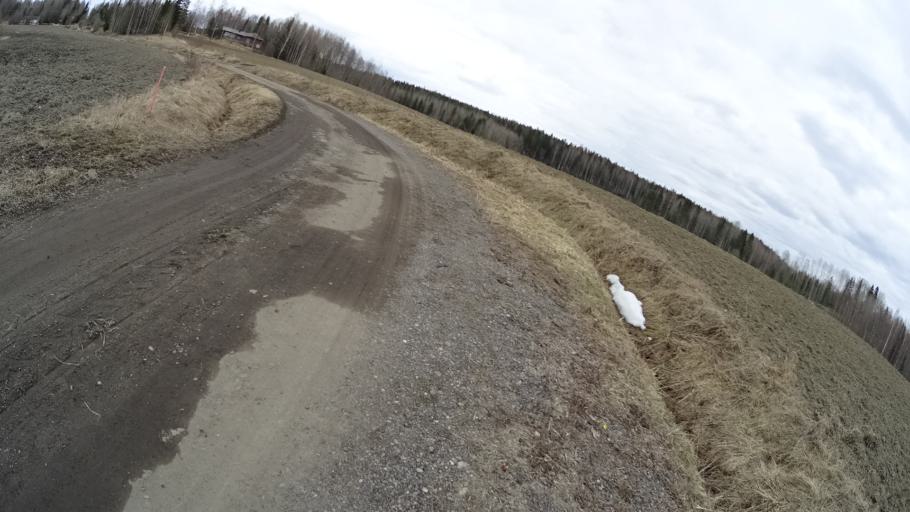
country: FI
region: Uusimaa
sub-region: Helsinki
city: Kilo
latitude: 60.2956
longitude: 24.7895
